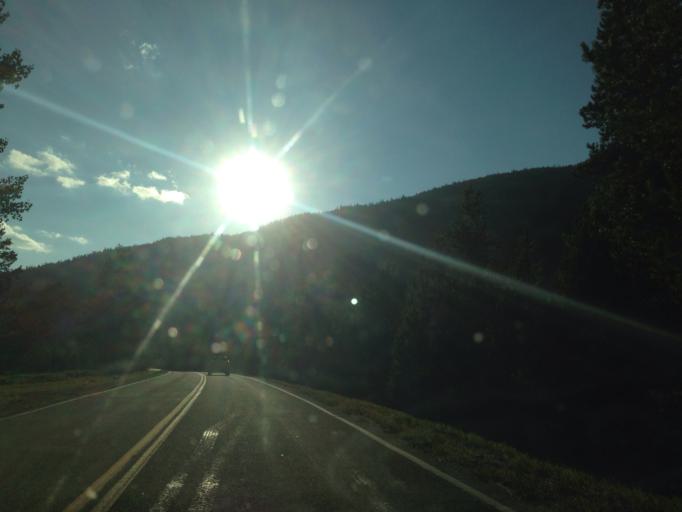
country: US
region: Utah
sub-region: Summit County
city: Francis
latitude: 40.5936
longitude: -111.0054
